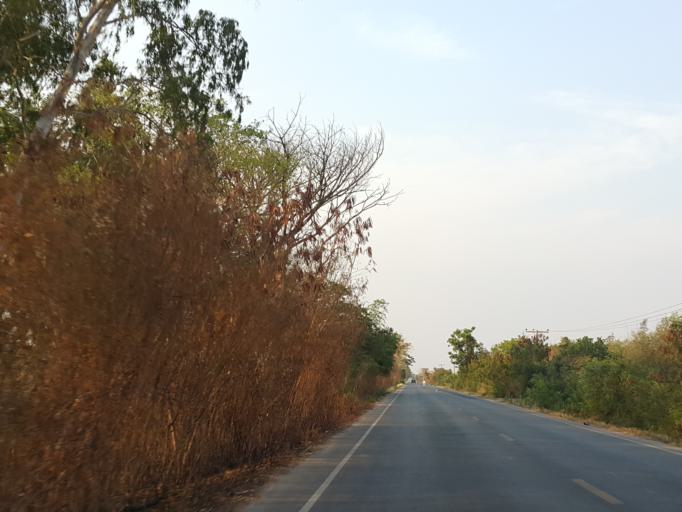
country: TH
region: Sukhothai
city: Si Samrong
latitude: 17.2145
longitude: 99.9494
